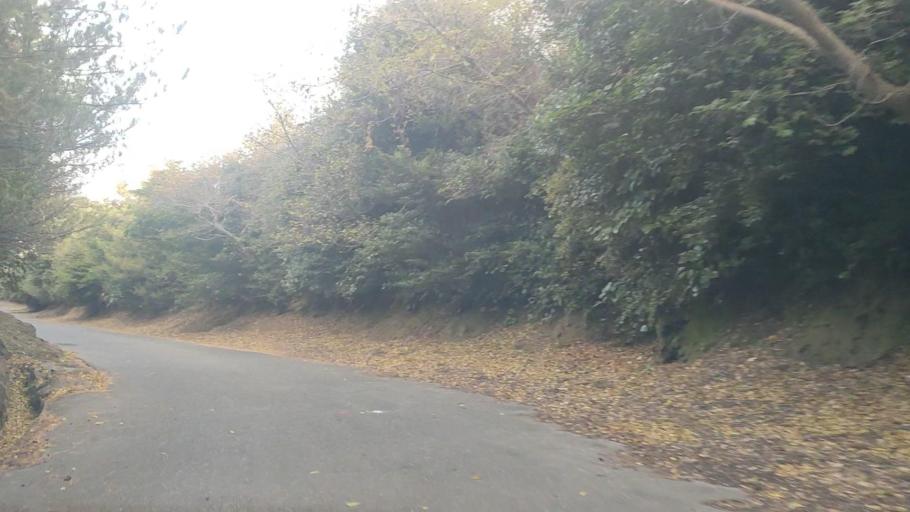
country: JP
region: Kagoshima
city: Kagoshima-shi
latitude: 31.5918
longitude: 130.6350
